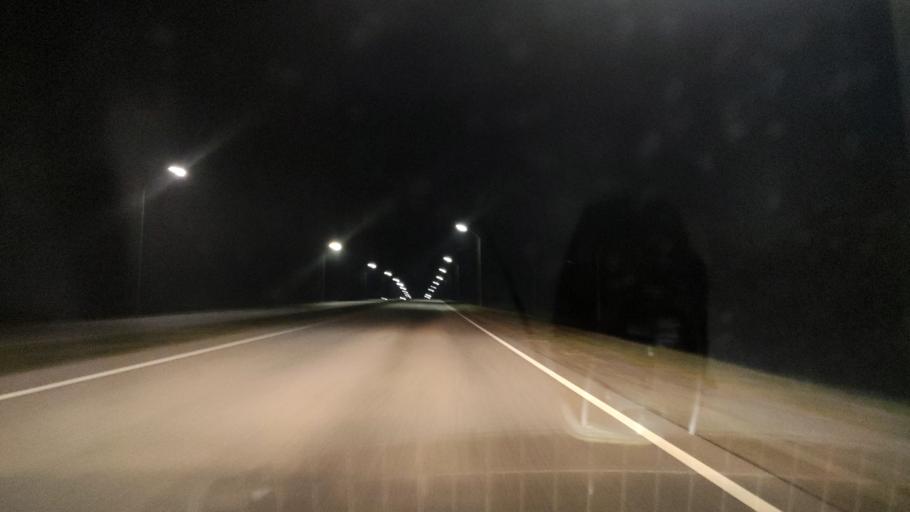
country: RU
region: Belgorod
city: Staryy Oskol
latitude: 51.3837
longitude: 37.8581
